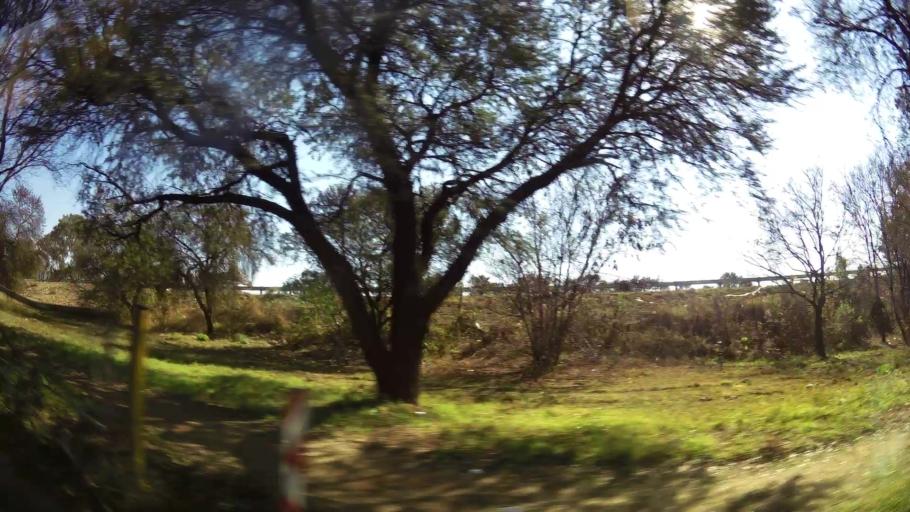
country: ZA
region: Gauteng
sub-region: City of Tshwane Metropolitan Municipality
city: Centurion
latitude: -25.8490
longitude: 28.1796
